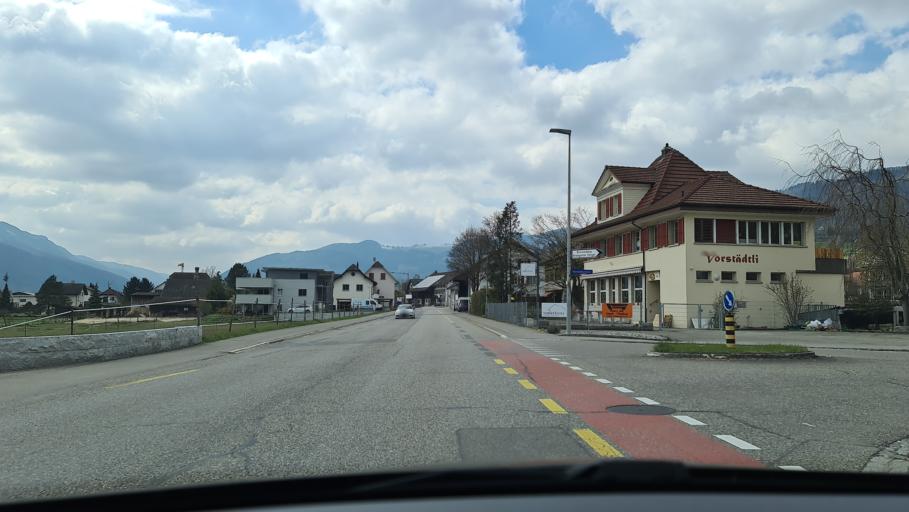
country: CH
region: Solothurn
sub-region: Bezirk Thal
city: Laupersdorf
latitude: 47.3120
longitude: 7.6552
